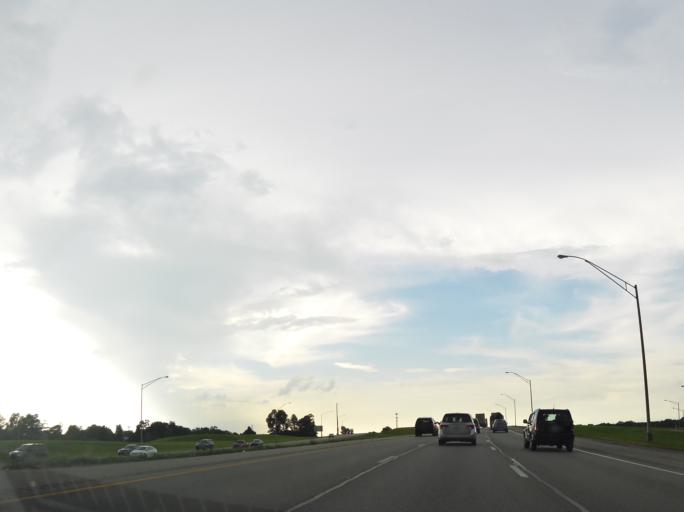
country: US
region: Kentucky
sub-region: Fayette County
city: Lexington-Fayette
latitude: 38.0510
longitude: -84.4277
